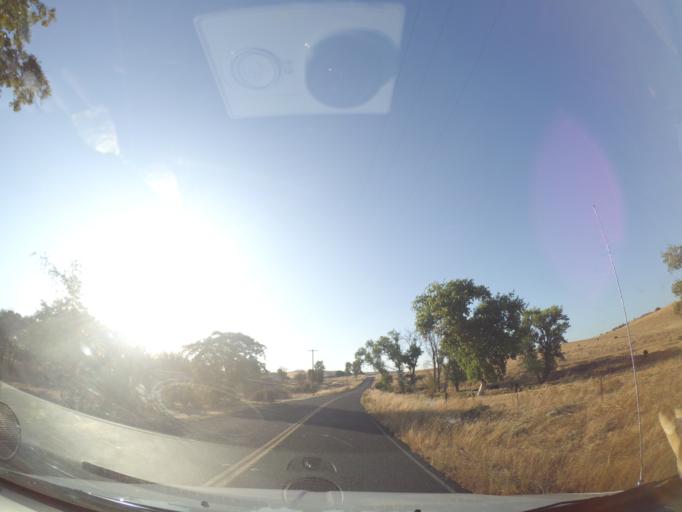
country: US
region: California
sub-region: Merced County
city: Planada
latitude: 37.4974
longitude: -120.2330
